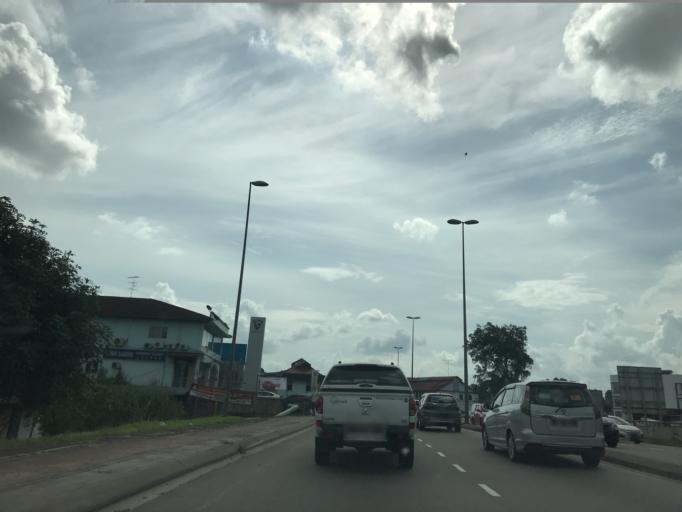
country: MY
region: Johor
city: Taman Senai
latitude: 1.6030
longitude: 103.6464
